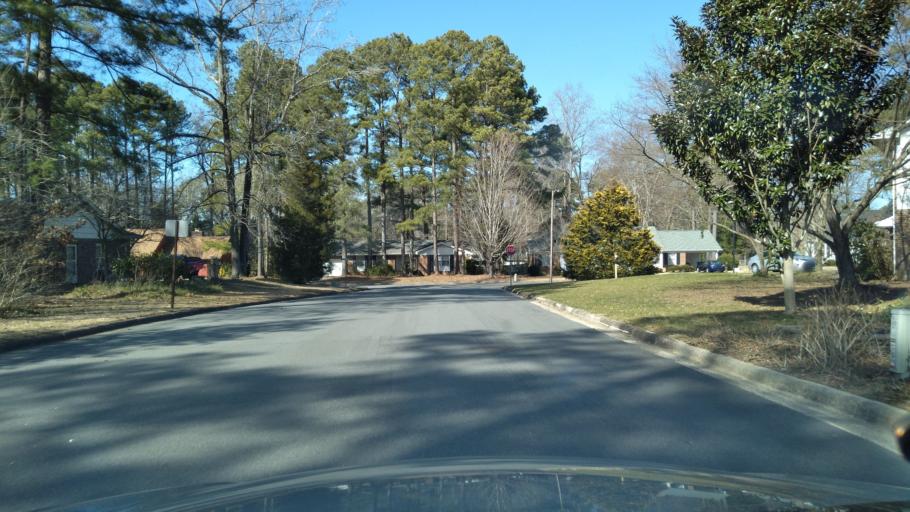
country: US
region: North Carolina
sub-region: Wake County
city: Garner
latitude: 35.6956
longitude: -78.6256
